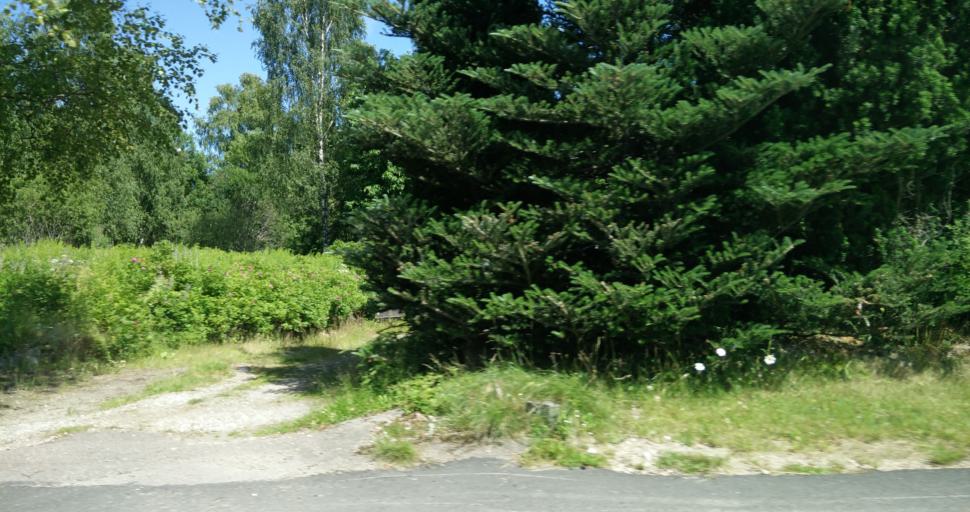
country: SE
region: Vaermland
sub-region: Hagfors Kommun
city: Hagfors
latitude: 60.0282
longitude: 13.6739
